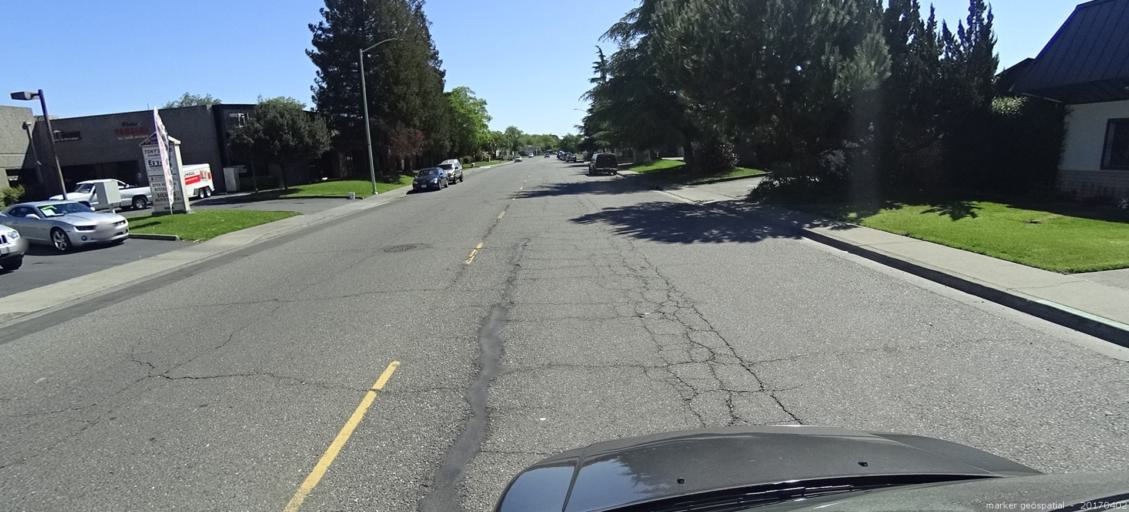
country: US
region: California
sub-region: Sacramento County
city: Parkway
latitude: 38.5024
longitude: -121.4652
